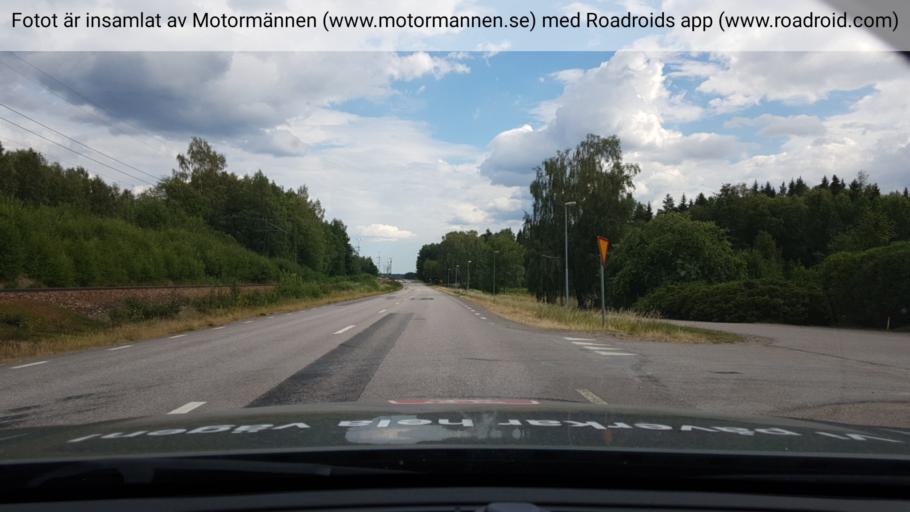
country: SE
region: Uppsala
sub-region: Heby Kommun
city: Morgongava
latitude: 59.9267
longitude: 16.9803
